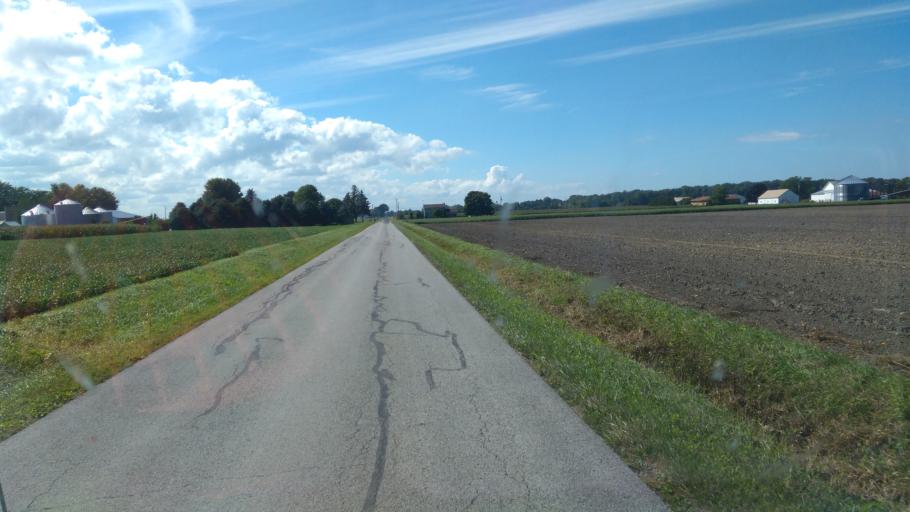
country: US
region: Ohio
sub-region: Ottawa County
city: Port Clinton
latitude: 41.4083
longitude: -82.8591
